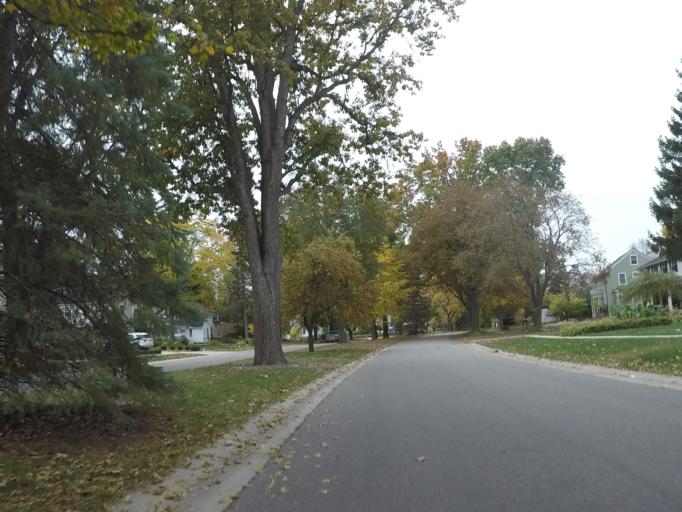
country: US
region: Wisconsin
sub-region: Dane County
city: Maple Bluff
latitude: 43.1091
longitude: -89.3671
